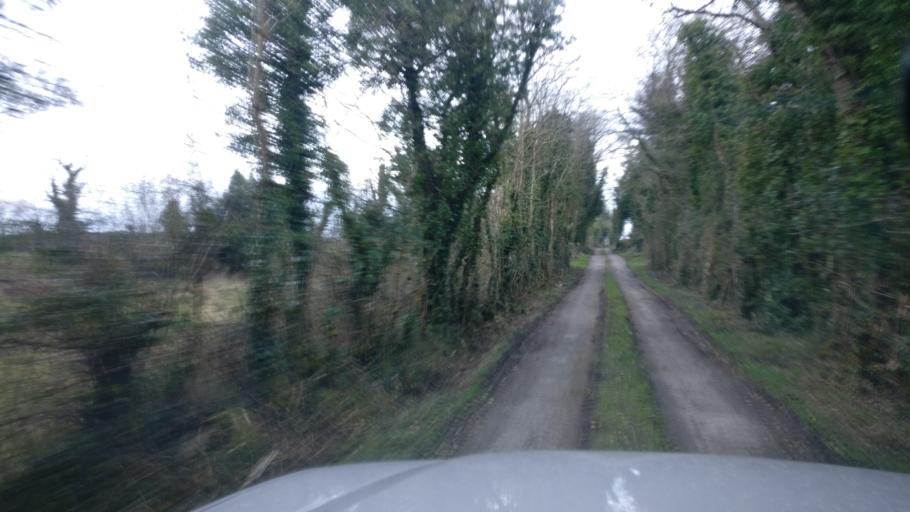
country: IE
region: Connaught
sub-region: County Galway
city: Loughrea
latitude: 53.2529
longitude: -8.4512
